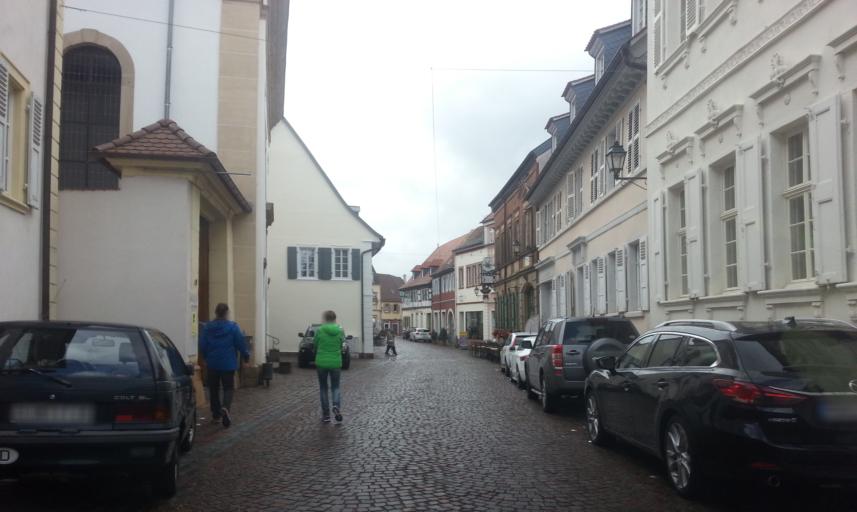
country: DE
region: Rheinland-Pfalz
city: Freinsheim
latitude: 49.5071
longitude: 8.2117
